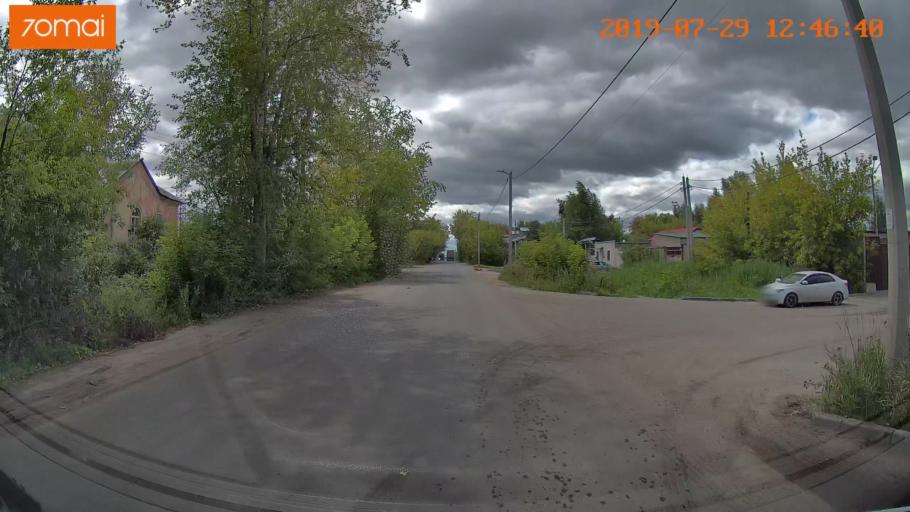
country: RU
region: Ivanovo
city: Novo-Talitsy
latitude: 56.9979
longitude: 40.9150
